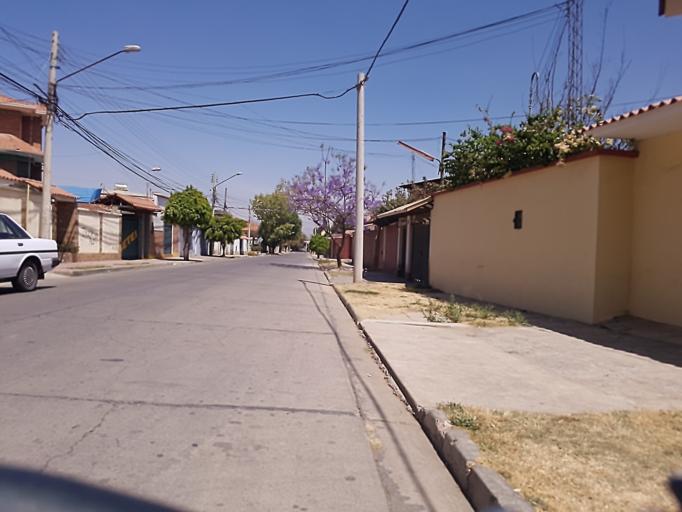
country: BO
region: Cochabamba
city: Cochabamba
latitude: -17.3673
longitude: -66.1817
